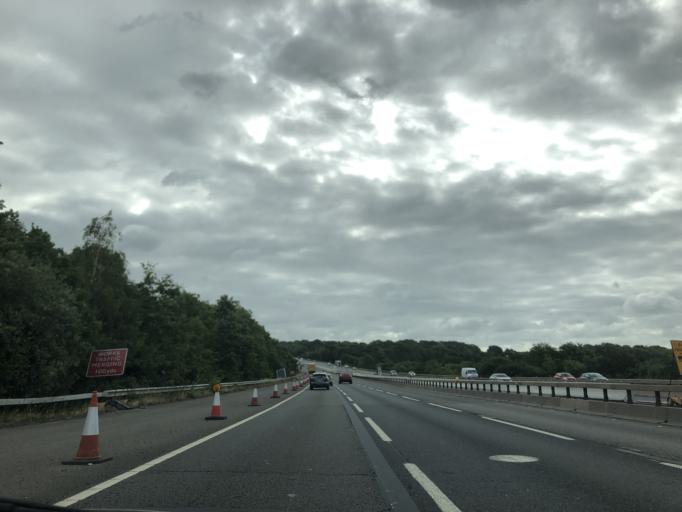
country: GB
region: England
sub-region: Hampshire
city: Wickham
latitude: 50.8680
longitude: -1.2280
